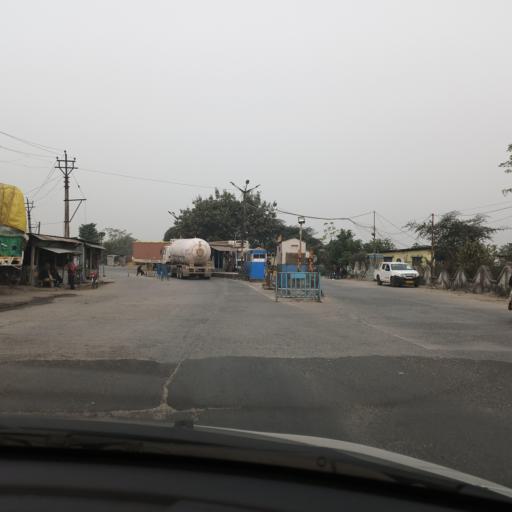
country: IN
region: West Bengal
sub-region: Darjiling
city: Shiliguri
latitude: 26.6574
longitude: 88.4151
